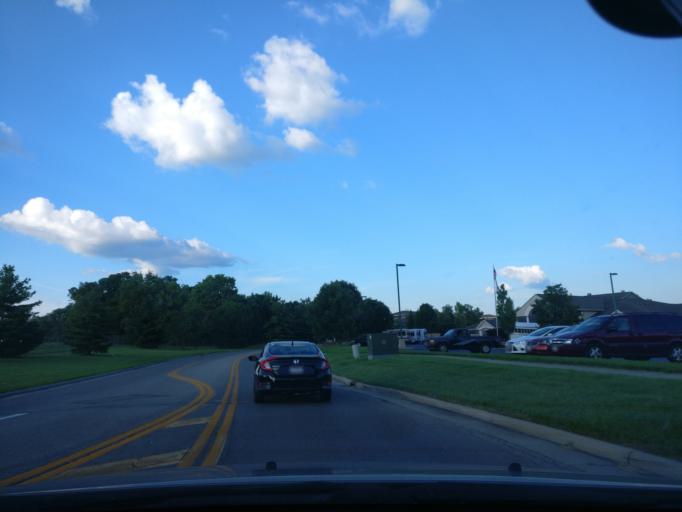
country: US
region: Ohio
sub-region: Warren County
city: Springboro
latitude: 39.5790
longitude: -84.2285
